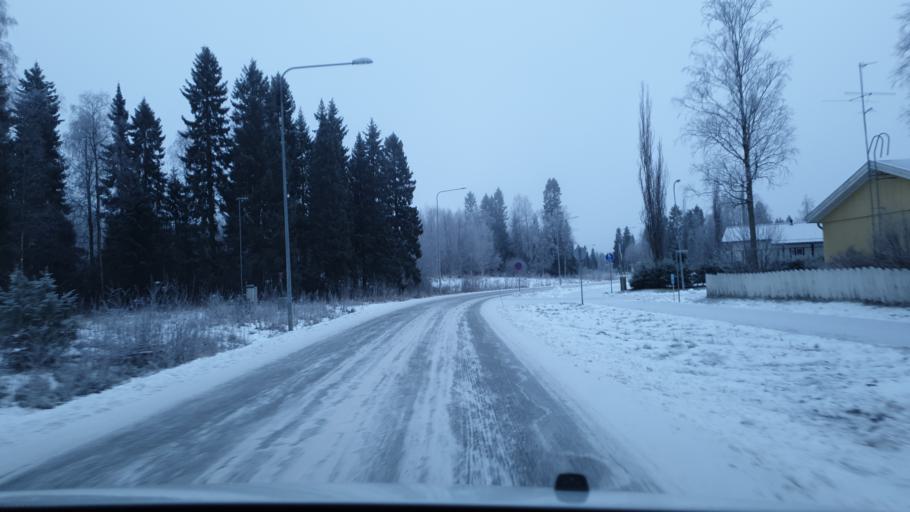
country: FI
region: Lapland
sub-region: Kemi-Tornio
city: Kemi
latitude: 65.7424
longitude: 24.6092
